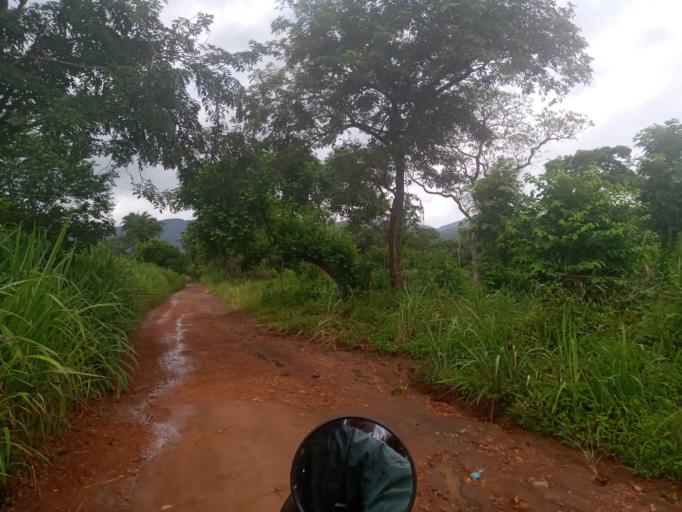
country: SL
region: Northern Province
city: Bumbuna
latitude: 8.9328
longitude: -11.7491
